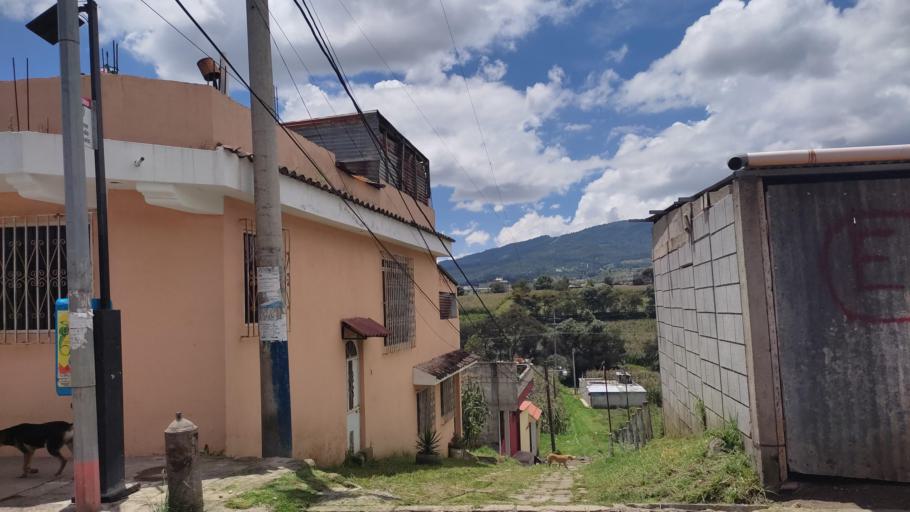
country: GT
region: Quetzaltenango
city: Olintepeque
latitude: 14.8618
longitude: -91.5322
